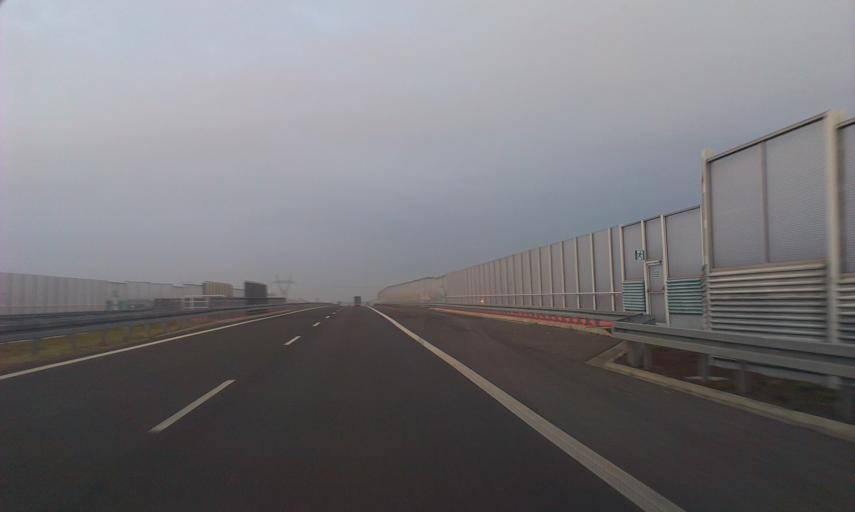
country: PL
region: Greater Poland Voivodeship
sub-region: Powiat poznanski
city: Rokietnica
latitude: 52.5038
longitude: 16.7686
